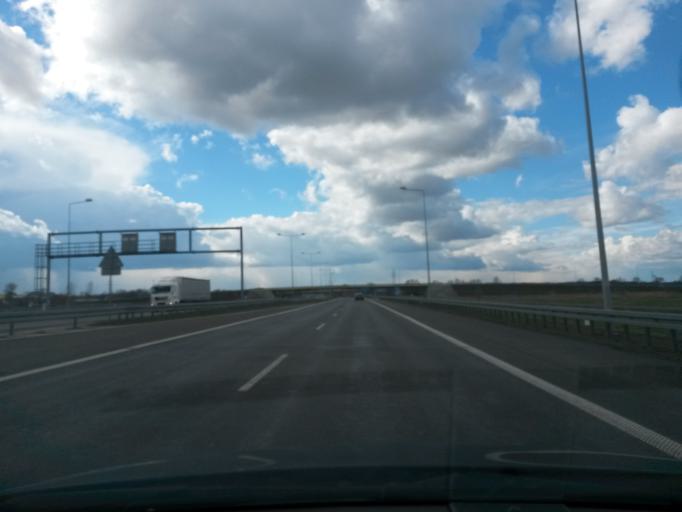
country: PL
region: Greater Poland Voivodeship
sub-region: Powiat turecki
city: Brudzew
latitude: 52.1391
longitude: 18.6181
